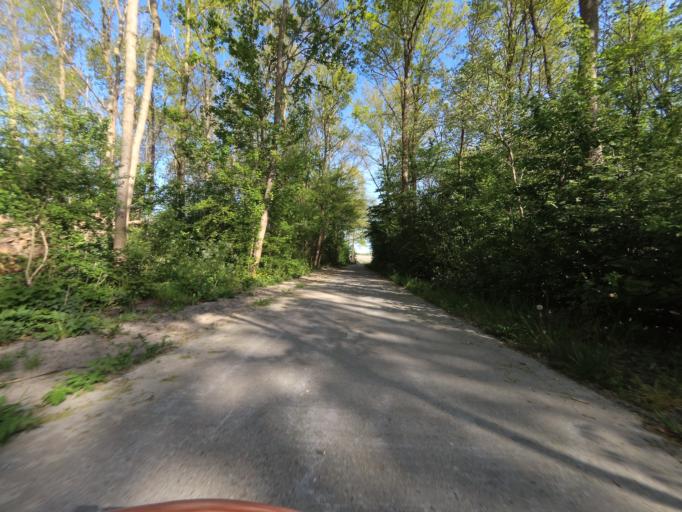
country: NL
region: Overijssel
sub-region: Gemeente Kampen
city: Kampen
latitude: 52.5214
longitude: 5.8562
